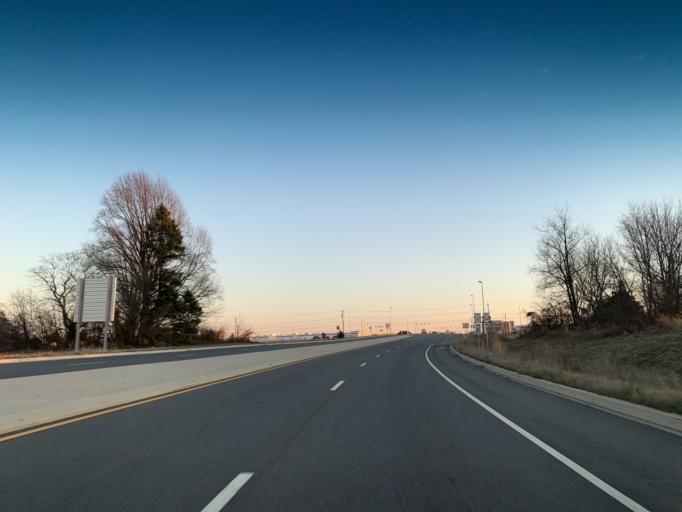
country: US
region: Delaware
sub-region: New Castle County
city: Middletown
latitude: 39.4429
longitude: -75.7487
